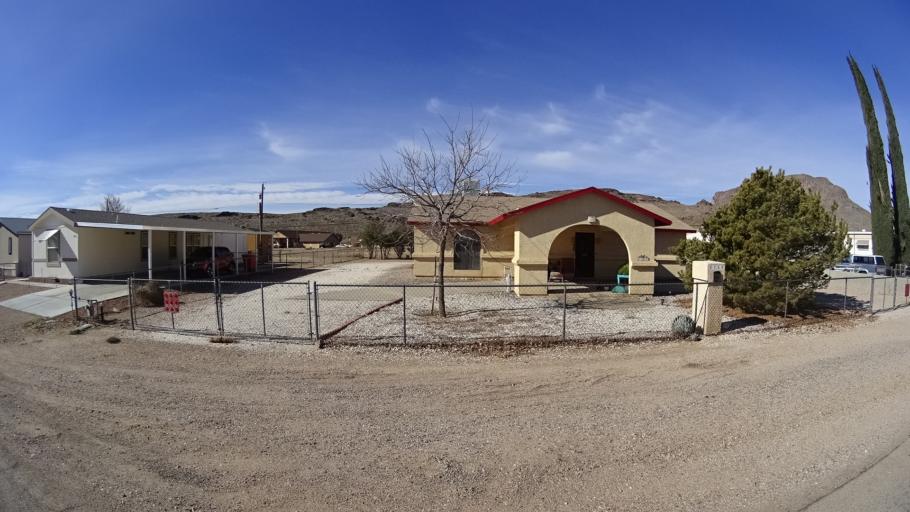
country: US
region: Arizona
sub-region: Mohave County
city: New Kingman-Butler
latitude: 35.2618
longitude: -114.0381
